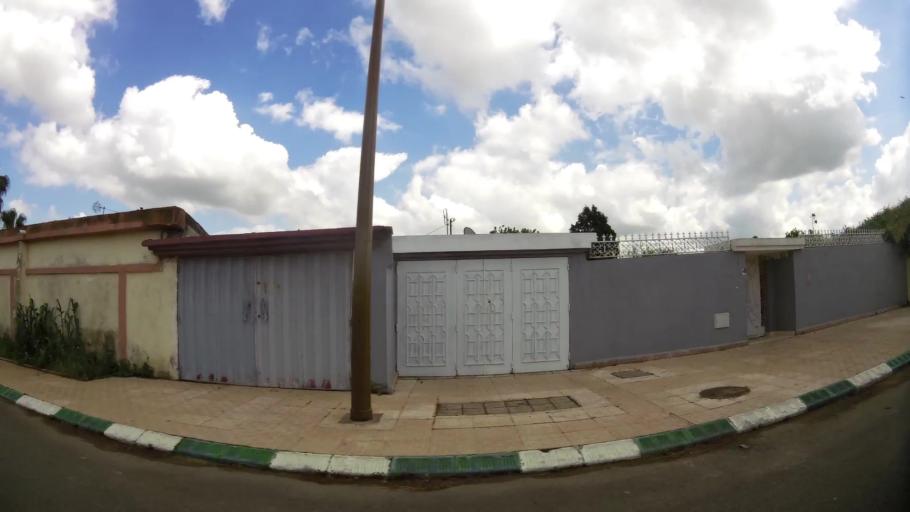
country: MA
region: Grand Casablanca
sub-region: Mediouna
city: Mediouna
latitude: 33.3853
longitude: -7.5404
